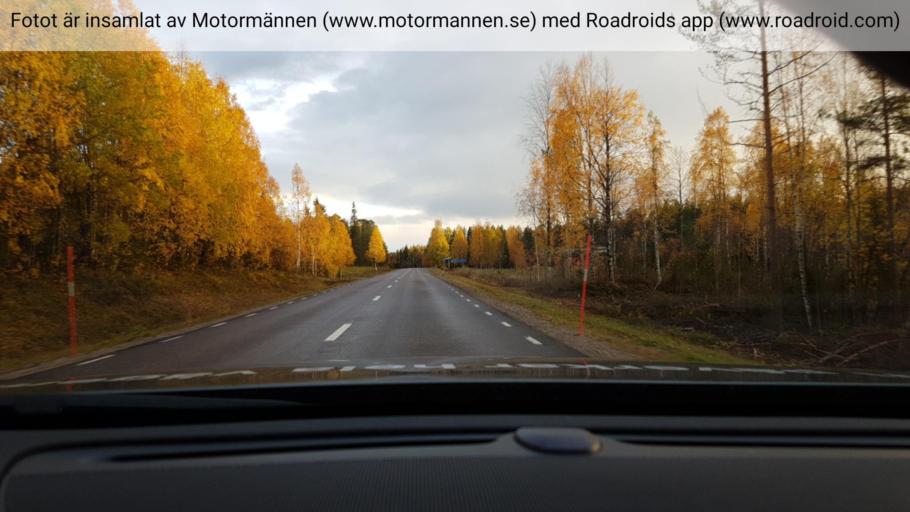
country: SE
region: Norrbotten
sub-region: Overkalix Kommun
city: OEverkalix
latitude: 66.5964
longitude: 22.7598
